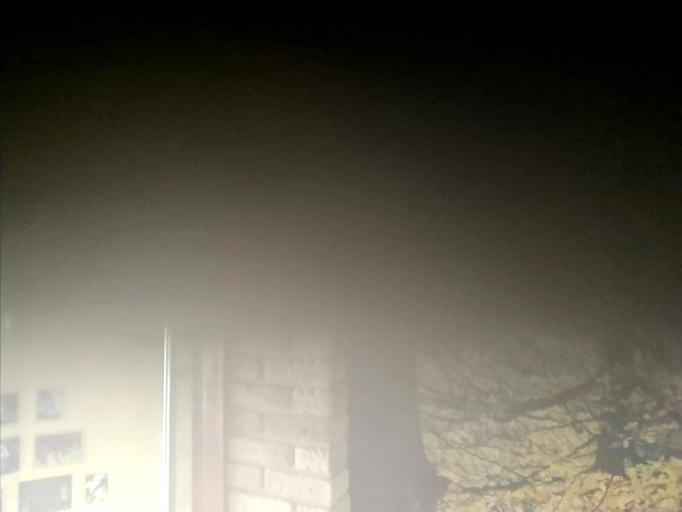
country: RU
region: Kaluga
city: Yukhnov
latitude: 54.6786
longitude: 35.0597
